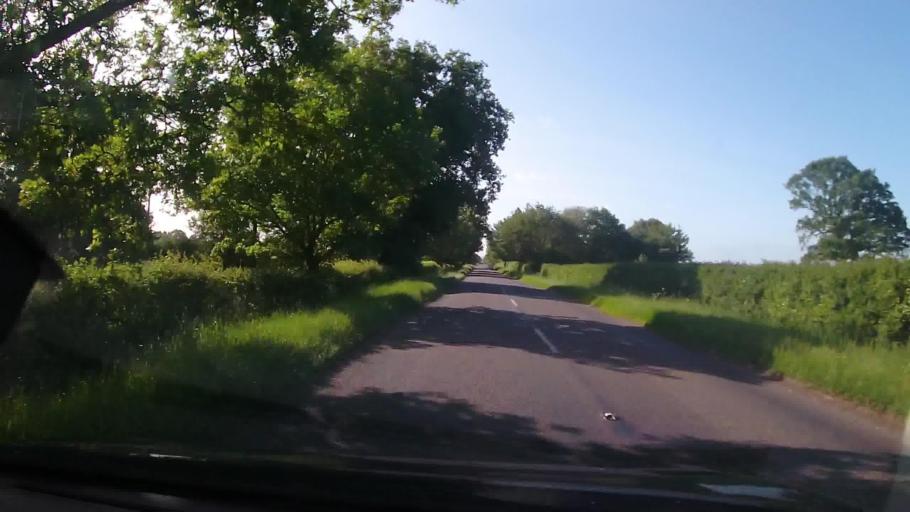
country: GB
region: England
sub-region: Shropshire
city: Shawbury
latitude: 52.7824
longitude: -2.6442
